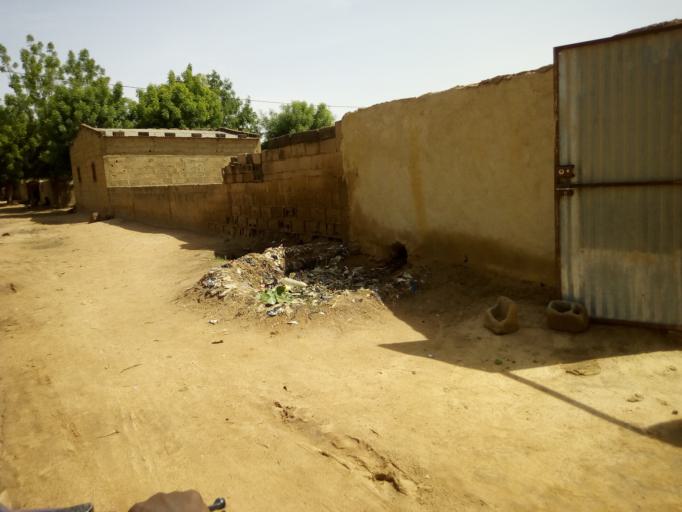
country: ML
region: Segou
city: Segou
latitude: 13.4313
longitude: -6.2096
